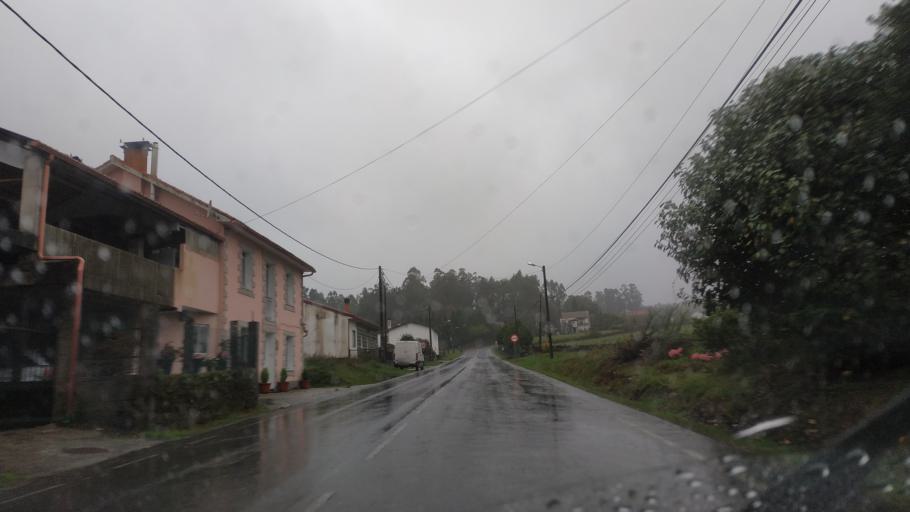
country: ES
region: Galicia
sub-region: Provincia da Coruna
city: Negreira
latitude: 42.9104
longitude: -8.7603
